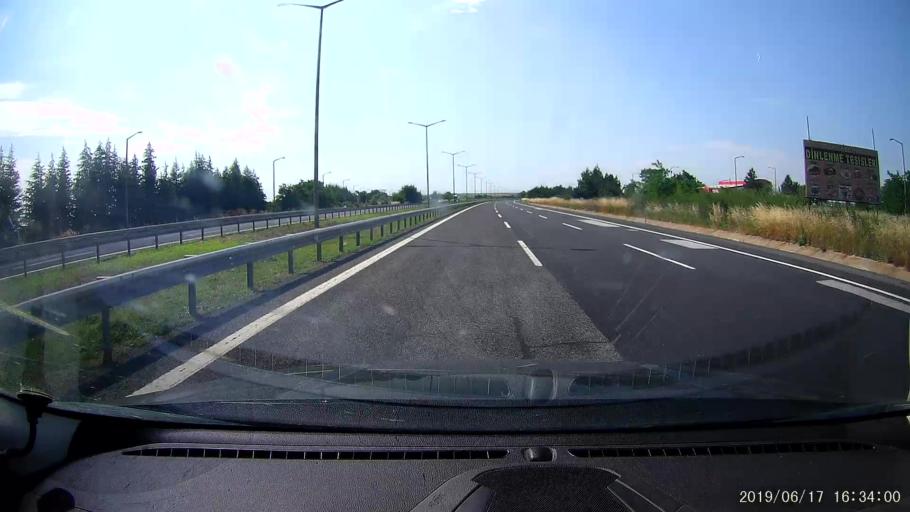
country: TR
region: Kirklareli
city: Buyukkaristiran
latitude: 41.3874
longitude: 27.5557
